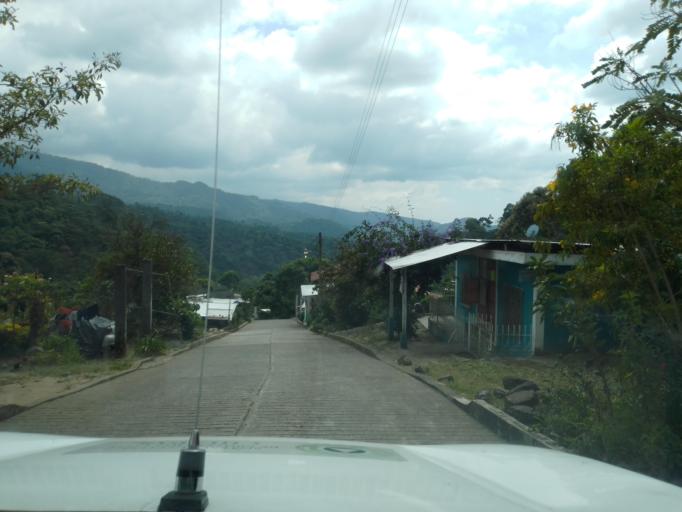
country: MX
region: Chiapas
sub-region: Union Juarez
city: Santo Domingo
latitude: 15.0586
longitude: -92.0938
